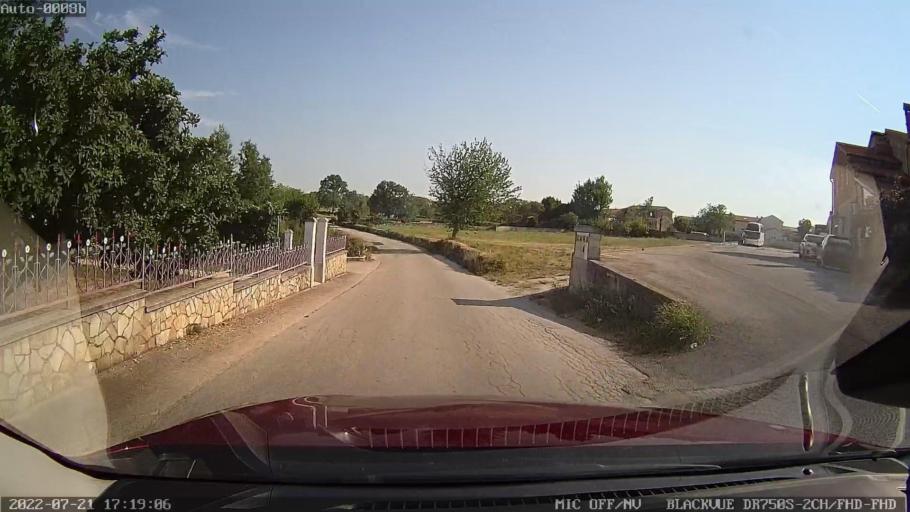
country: HR
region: Istarska
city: Karojba
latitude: 45.2139
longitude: 13.8251
